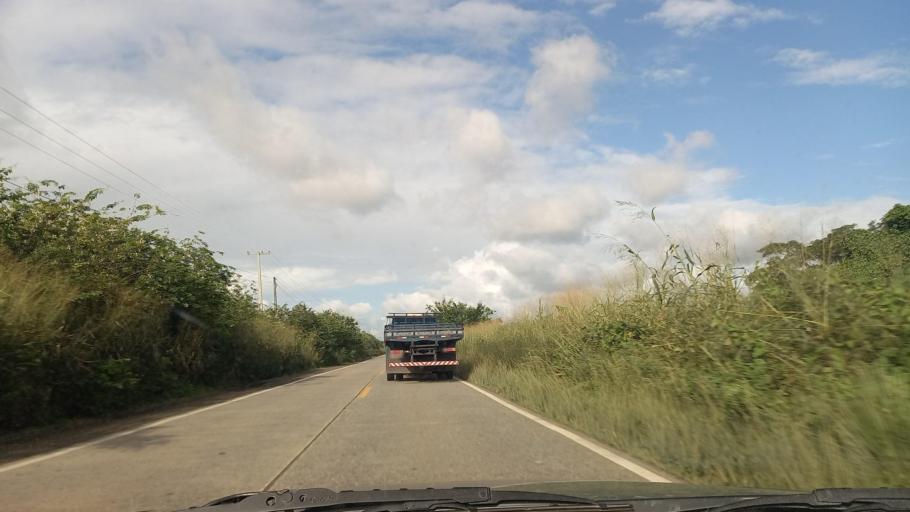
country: BR
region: Pernambuco
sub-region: Palmares
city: Palmares
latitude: -8.6914
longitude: -35.6267
